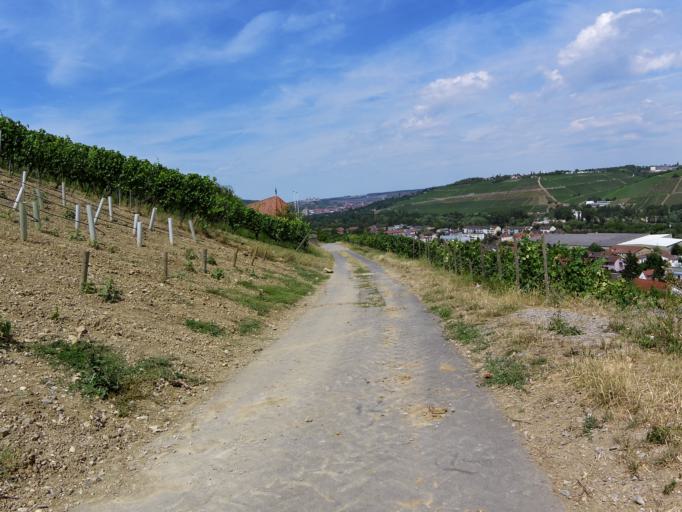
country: DE
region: Bavaria
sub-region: Regierungsbezirk Unterfranken
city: Randersacker
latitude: 49.7559
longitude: 9.9628
